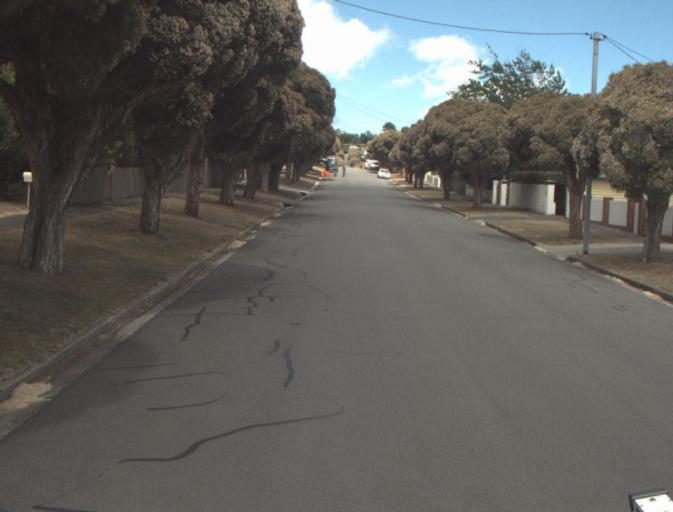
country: AU
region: Tasmania
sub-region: Launceston
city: Newstead
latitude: -41.4441
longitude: 147.1617
